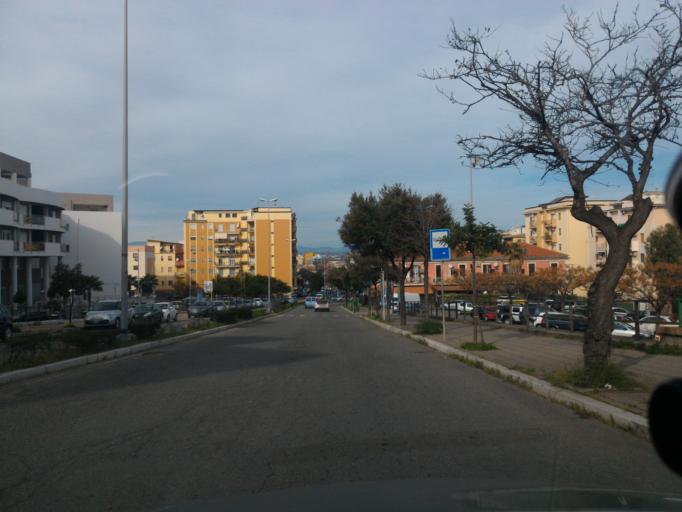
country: IT
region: Calabria
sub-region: Provincia di Crotone
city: Crotone
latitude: 39.0766
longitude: 17.1260
